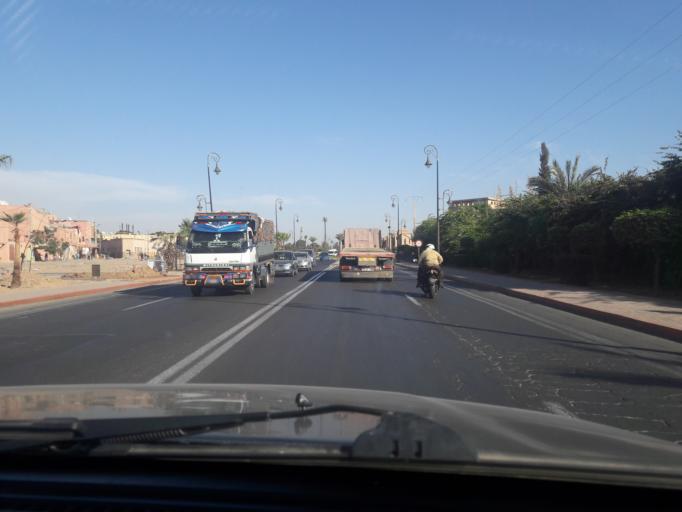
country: MA
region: Marrakech-Tensift-Al Haouz
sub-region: Marrakech
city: Marrakesh
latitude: 31.6483
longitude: -7.9536
